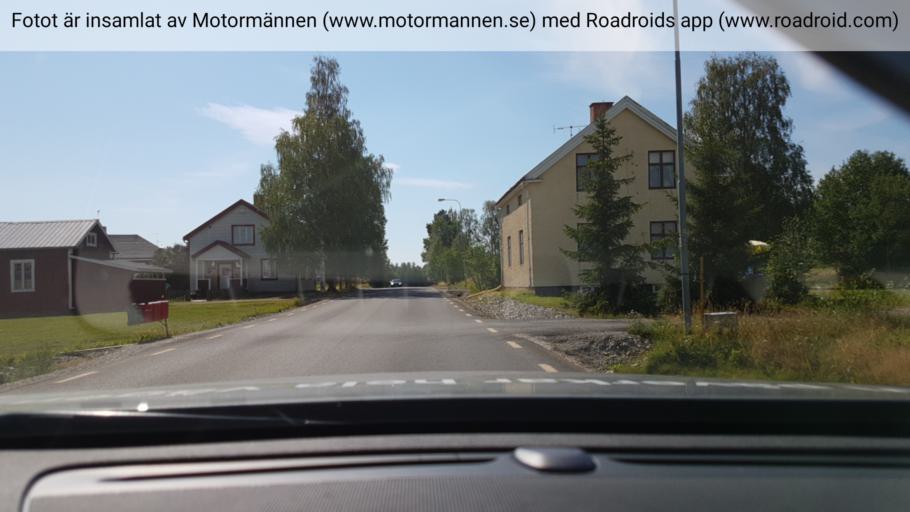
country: SE
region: Vaesterbotten
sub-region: Norsjo Kommun
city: Norsjoe
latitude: 64.5252
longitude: 19.3471
